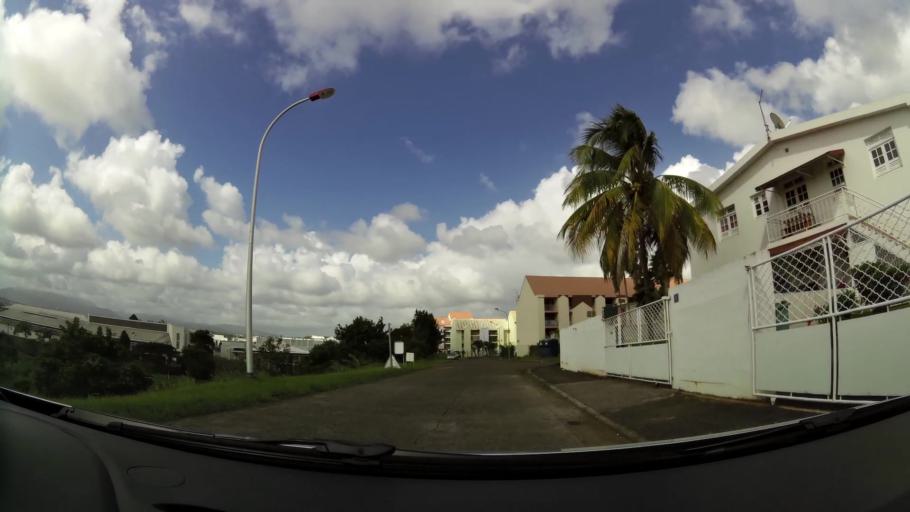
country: MQ
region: Martinique
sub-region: Martinique
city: Le Lamentin
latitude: 14.6148
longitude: -60.9878
